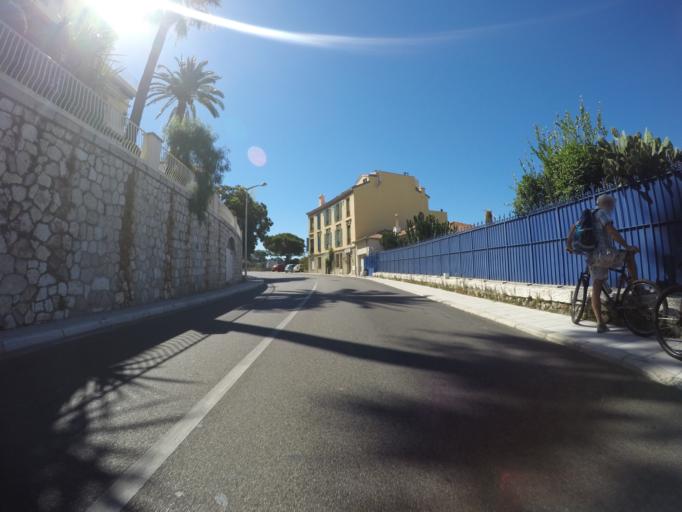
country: FR
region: Provence-Alpes-Cote d'Azur
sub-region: Departement des Alpes-Maritimes
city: Villefranche-sur-Mer
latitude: 43.6928
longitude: 7.2933
